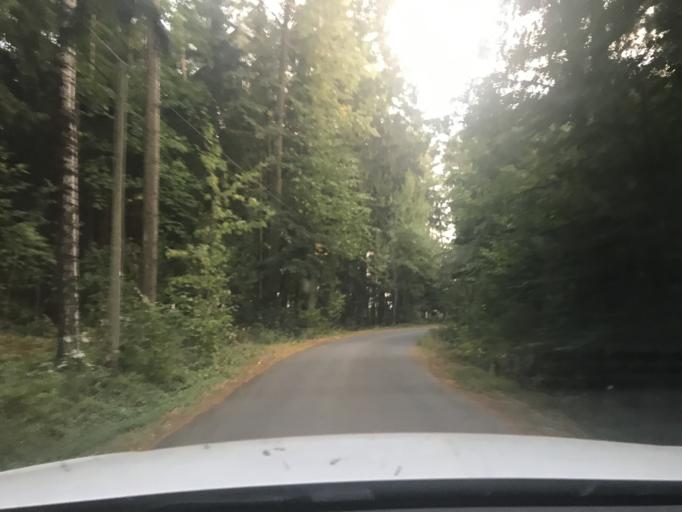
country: DE
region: Bavaria
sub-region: Upper Franconia
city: Emtmannsberg
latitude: 49.8963
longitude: 11.6173
